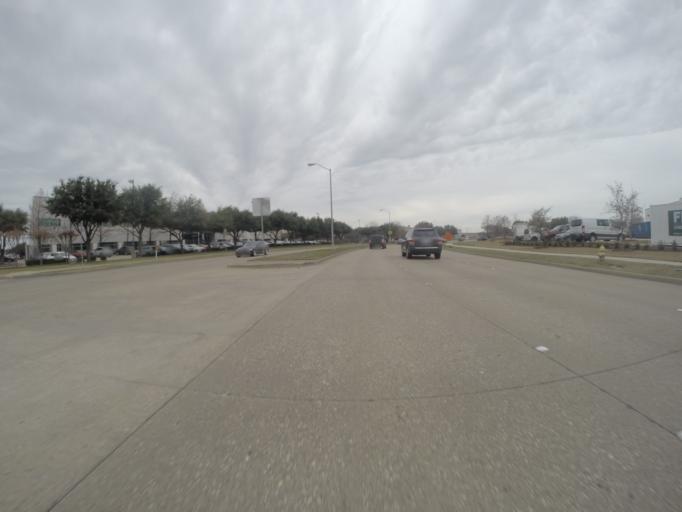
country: US
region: Texas
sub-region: Collin County
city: Saint Paul
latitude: 33.0308
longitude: -96.5615
